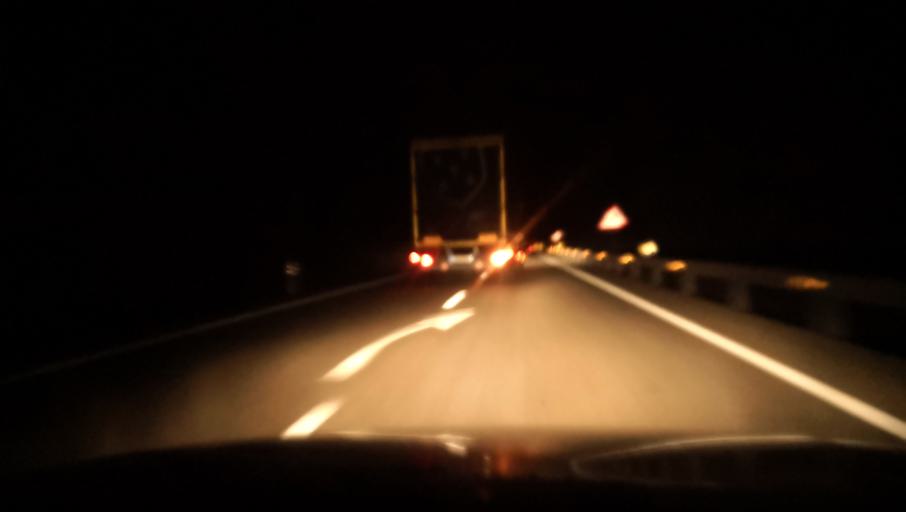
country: ES
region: Castille and Leon
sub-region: Provincia de Zamora
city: Alcanices
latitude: 41.7048
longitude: -6.3696
